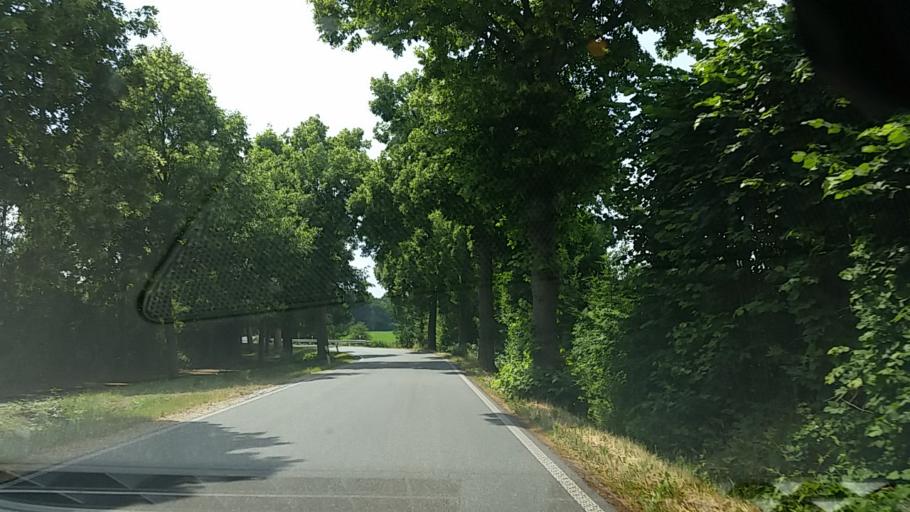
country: DE
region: Schleswig-Holstein
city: Tremsbuttel
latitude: 53.7366
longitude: 10.2954
